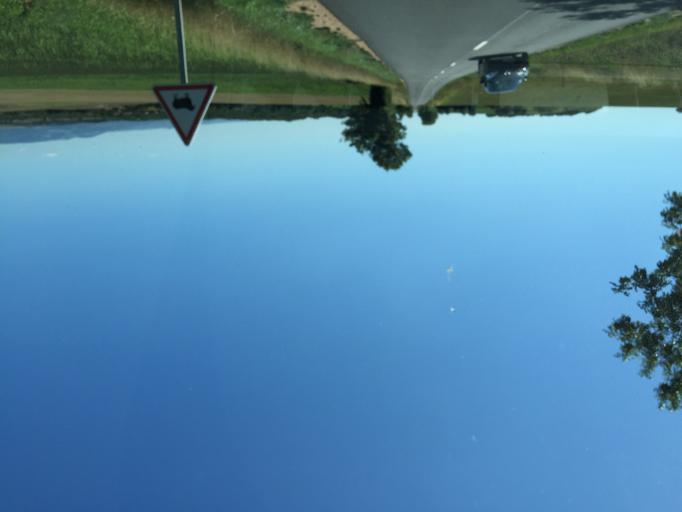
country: FR
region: Midi-Pyrenees
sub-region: Departement de l'Aveyron
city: Creissels
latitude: 44.0158
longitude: 3.0809
